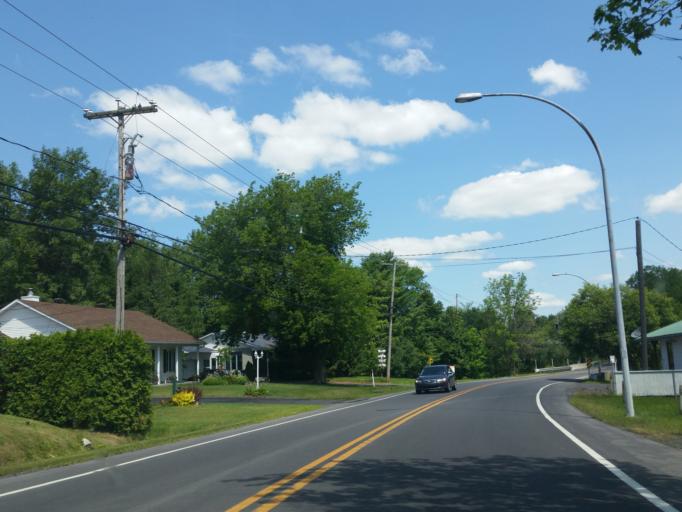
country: CA
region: Quebec
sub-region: Monteregie
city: Saint-Jean-sur-Richelieu
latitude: 45.3587
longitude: -73.2688
